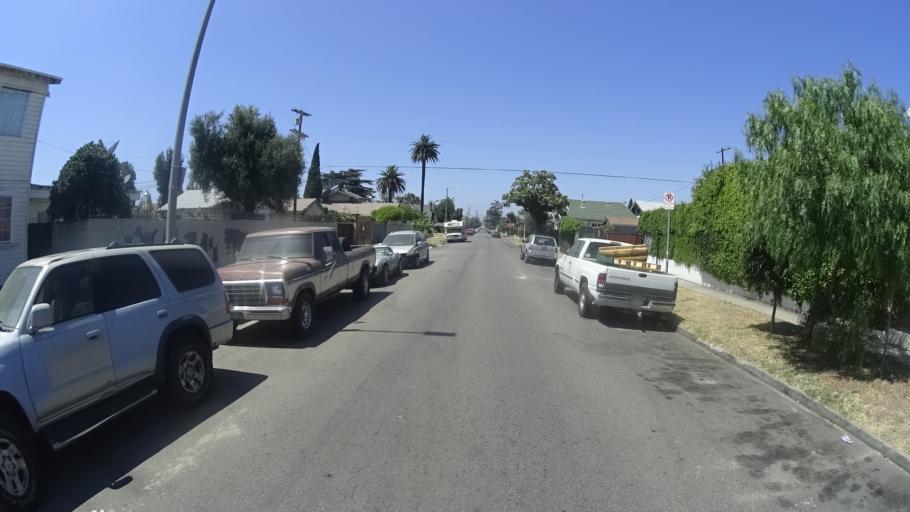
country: US
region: California
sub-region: Los Angeles County
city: View Park-Windsor Hills
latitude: 34.0008
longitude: -118.2937
